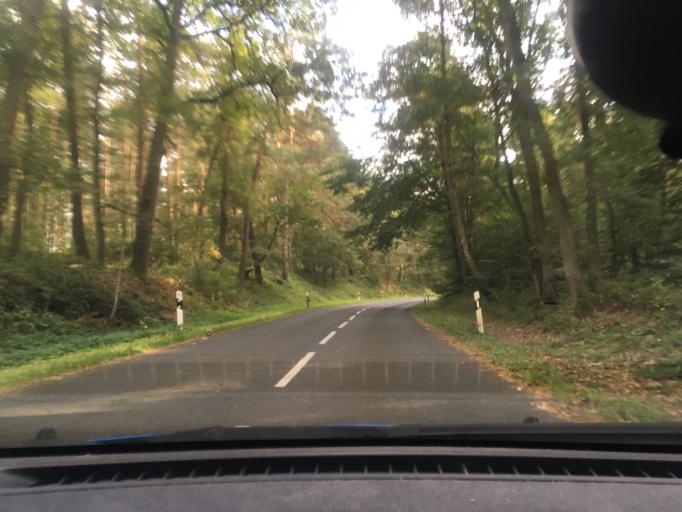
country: DE
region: Lower Saxony
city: Gohrde
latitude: 53.1557
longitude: 10.8676
